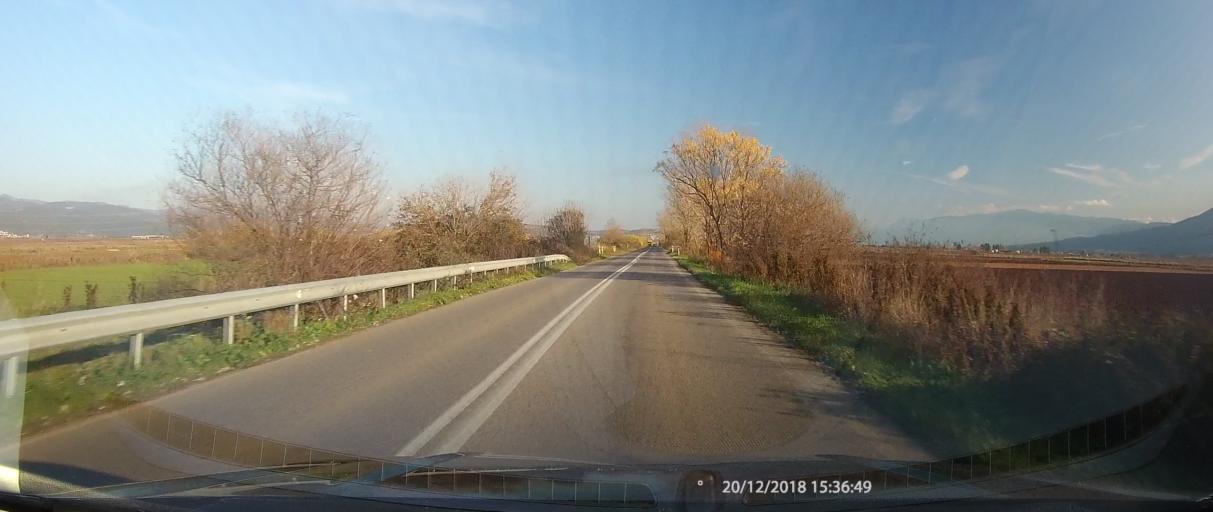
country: GR
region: Central Greece
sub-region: Nomos Fthiotidos
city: Lianokladhion
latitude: 38.9149
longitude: 22.3166
